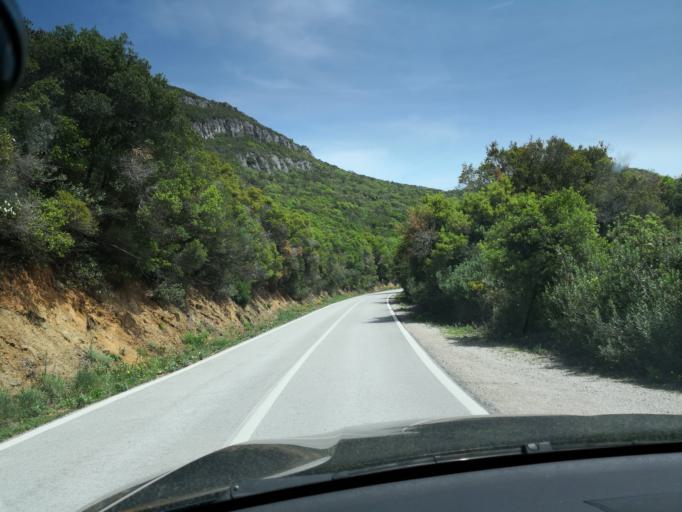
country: PT
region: Setubal
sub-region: Sesimbra
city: Sesimbra
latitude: 38.4704
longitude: -9.0019
